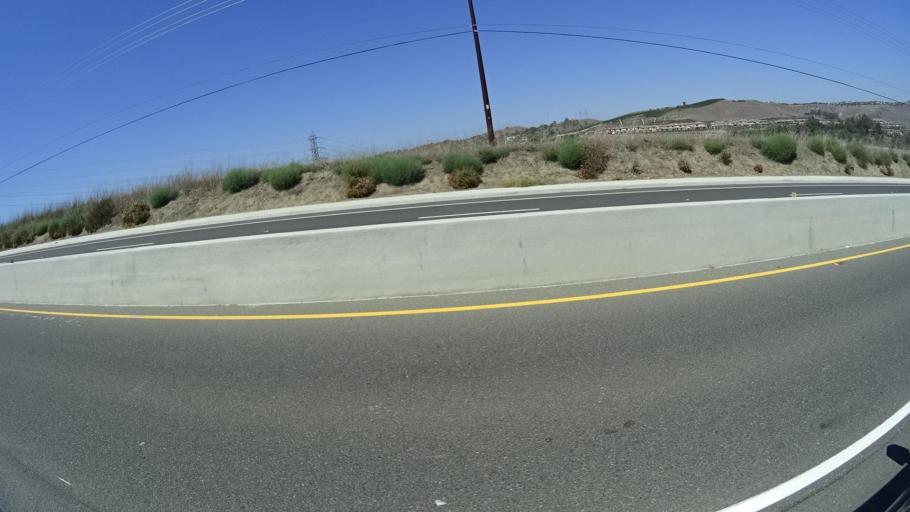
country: US
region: California
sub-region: Orange County
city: San Juan Capistrano
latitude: 33.5132
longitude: -117.6218
